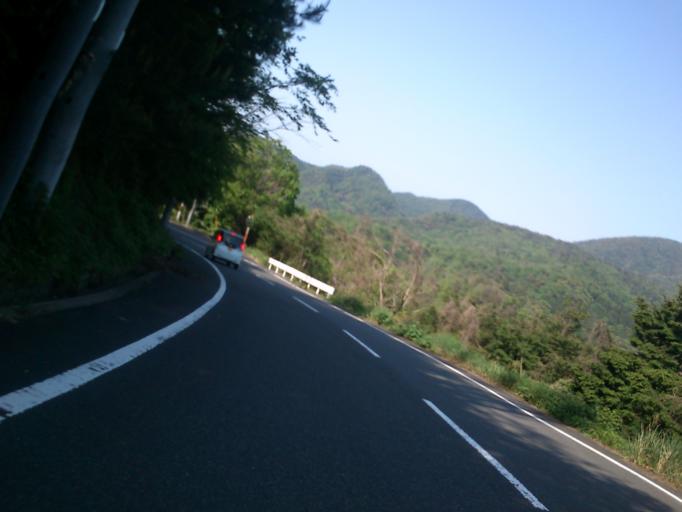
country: JP
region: Kyoto
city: Miyazu
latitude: 35.7411
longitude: 135.1746
